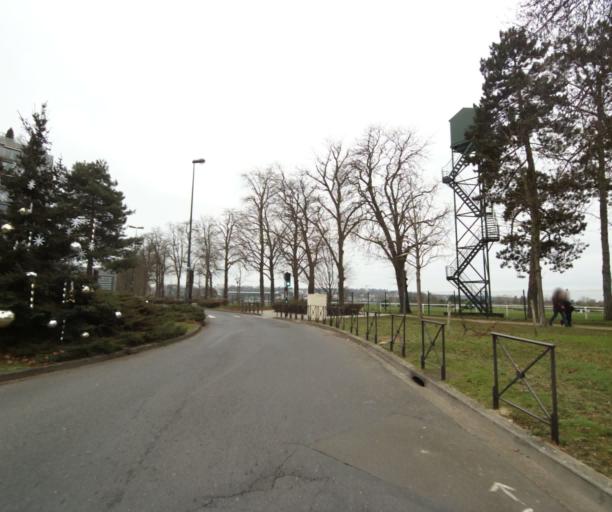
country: FR
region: Ile-de-France
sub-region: Departement des Hauts-de-Seine
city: Saint-Cloud
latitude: 48.8581
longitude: 2.2108
